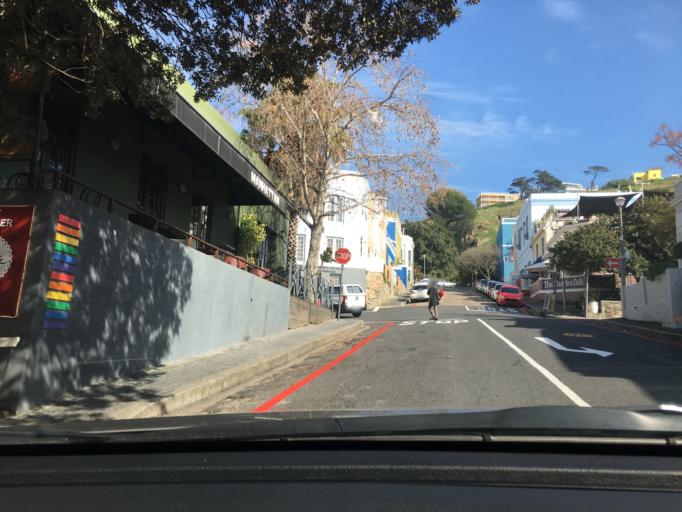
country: ZA
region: Western Cape
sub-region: City of Cape Town
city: Cape Town
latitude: -33.9163
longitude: 18.4175
